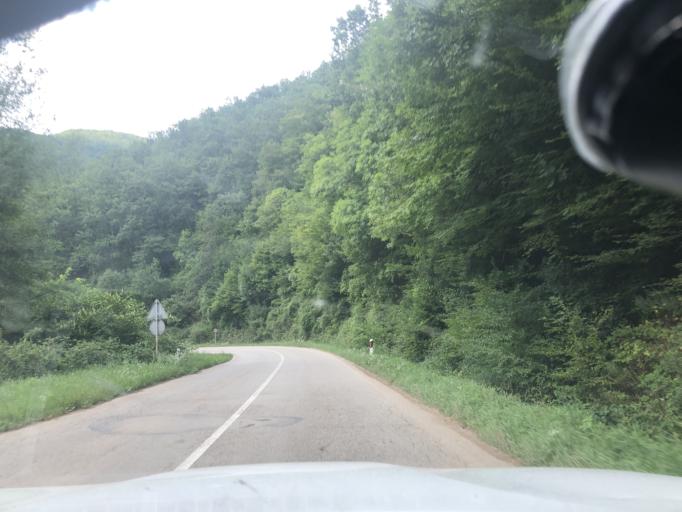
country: RS
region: Central Serbia
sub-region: Jablanicki Okrug
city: Medvega
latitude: 42.7805
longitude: 21.5973
